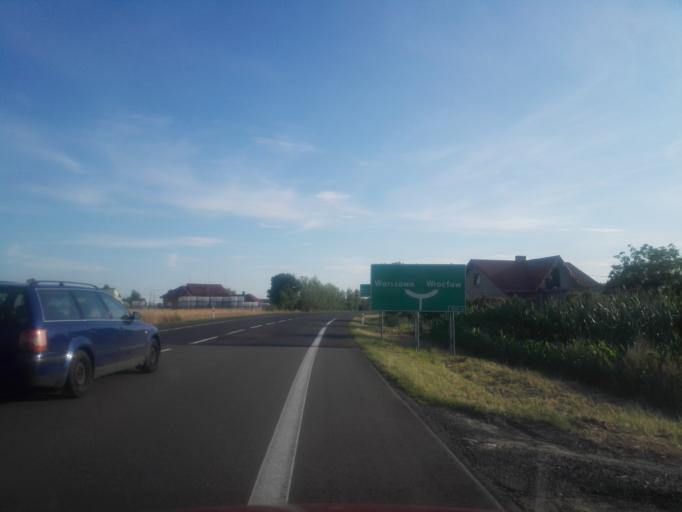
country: PL
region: Lodz Voivodeship
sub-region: Powiat wieruszowski
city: Walichnowy
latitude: 51.3099
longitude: 18.3823
